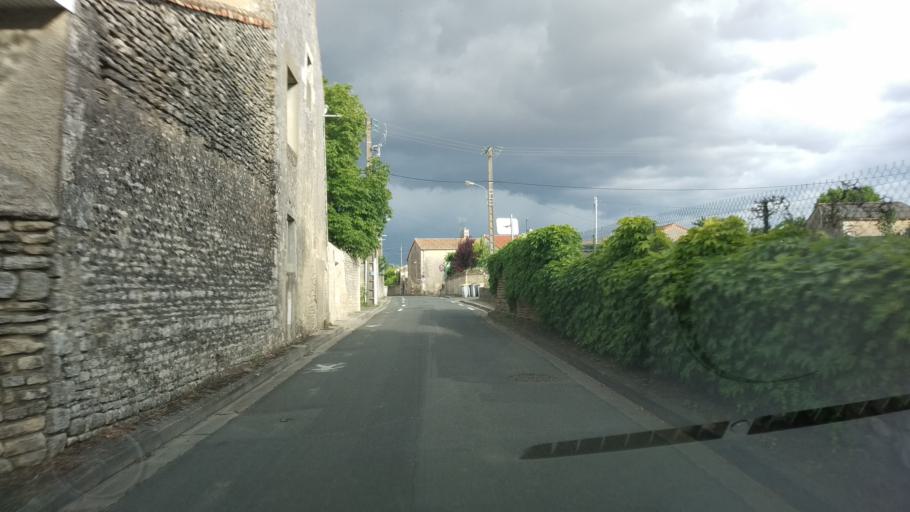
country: FR
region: Poitou-Charentes
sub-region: Departement de la Vienne
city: Migne-Auxances
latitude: 46.6288
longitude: 0.3353
